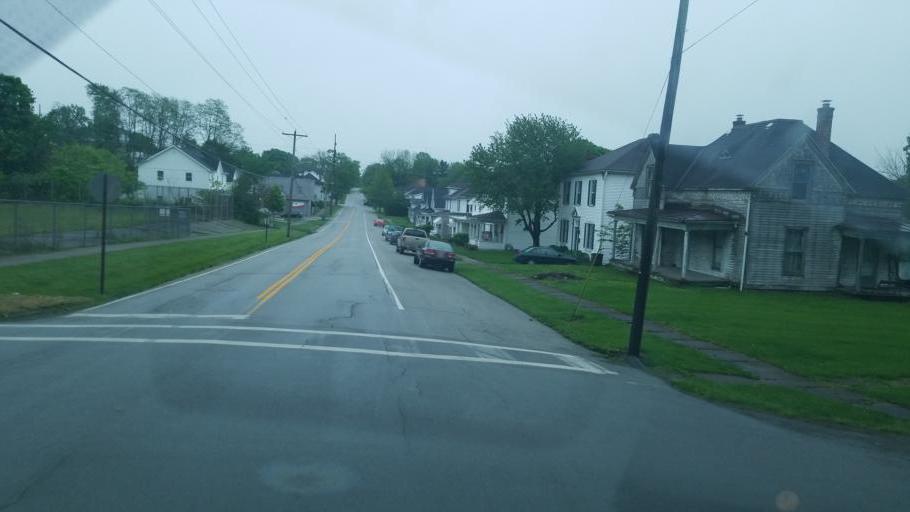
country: US
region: Ohio
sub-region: Highland County
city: Hillsboro
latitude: 39.2003
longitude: -83.6175
